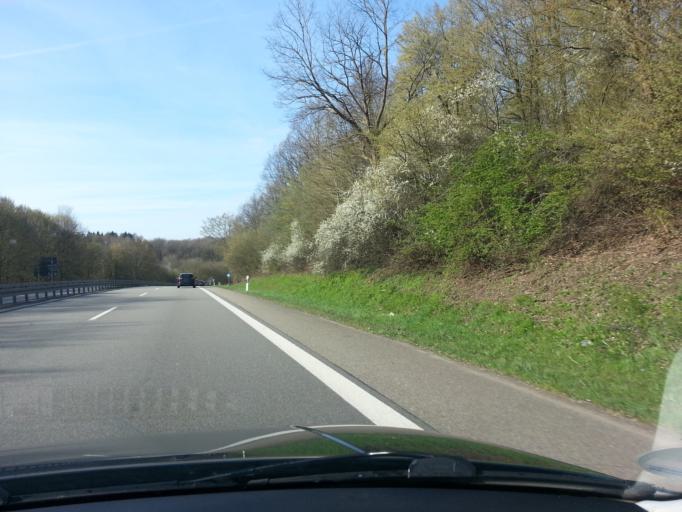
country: DE
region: Saarland
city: Sulzbach
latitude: 49.2856
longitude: 7.0179
